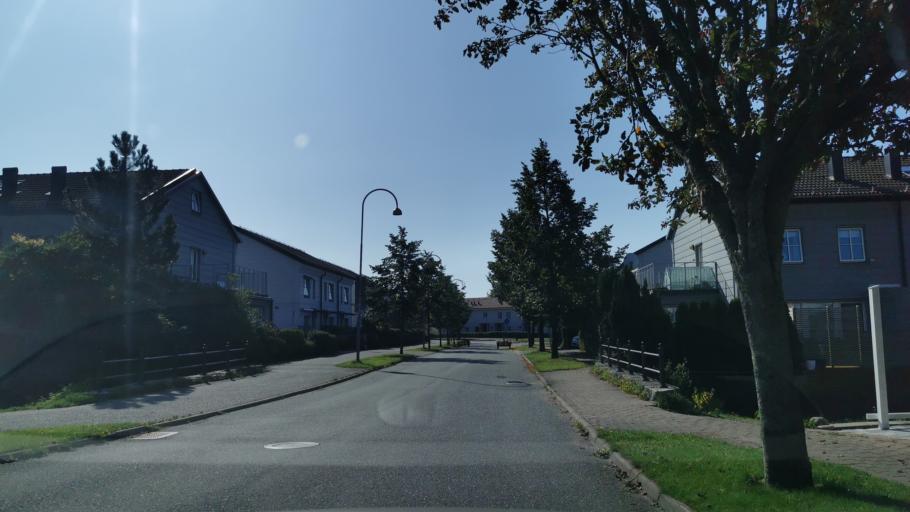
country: SE
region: Vaestra Goetaland
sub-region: Molndal
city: Moelndal
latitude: 57.6549
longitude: 11.9621
